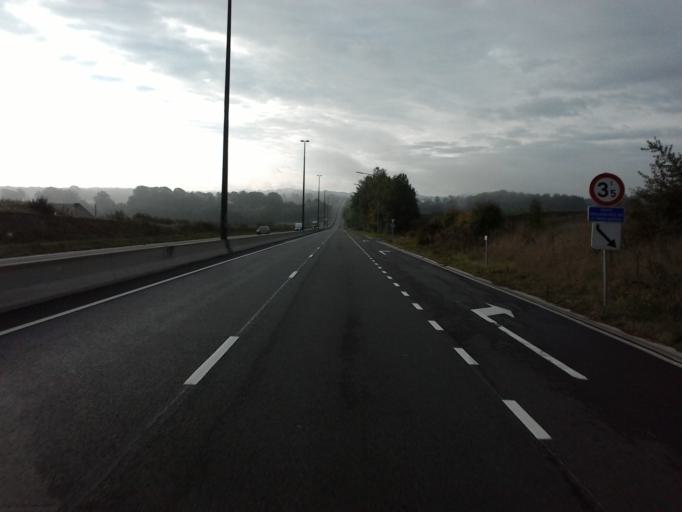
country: BE
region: Wallonia
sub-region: Province du Luxembourg
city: Attert
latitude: 49.7515
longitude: 5.7795
